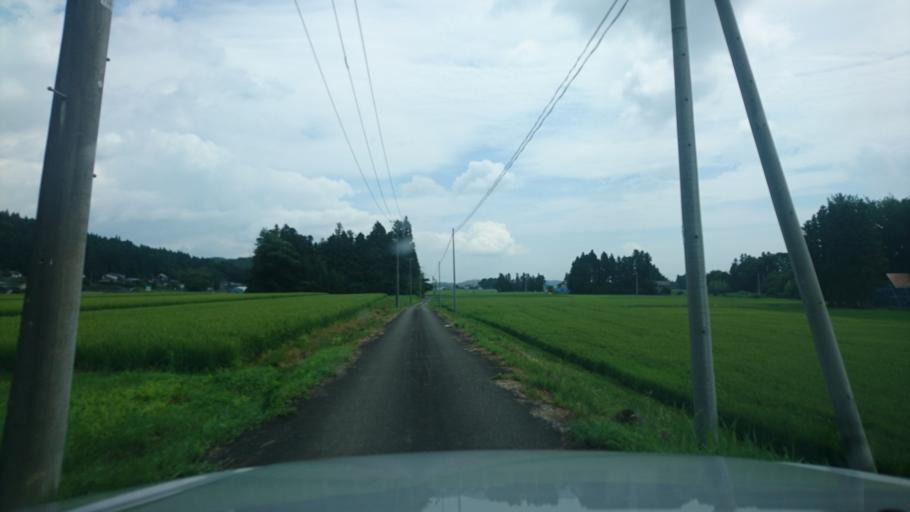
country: JP
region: Iwate
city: Ichinoseki
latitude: 38.8231
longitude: 140.9243
